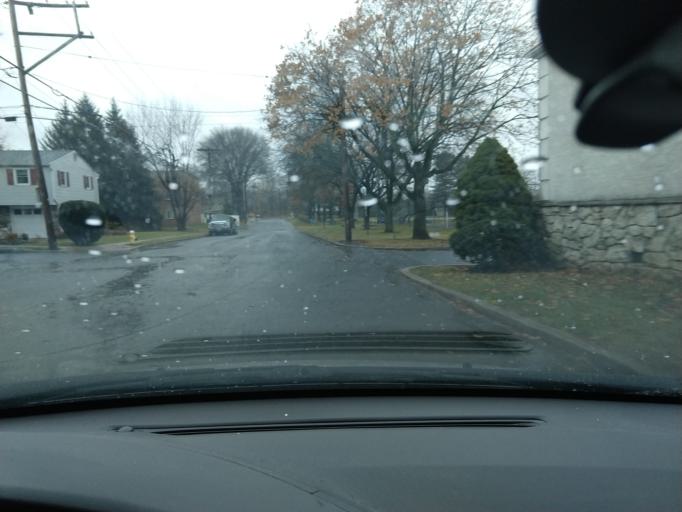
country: US
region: Pennsylvania
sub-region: Chester County
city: Kenilworth
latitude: 40.2390
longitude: -75.6203
